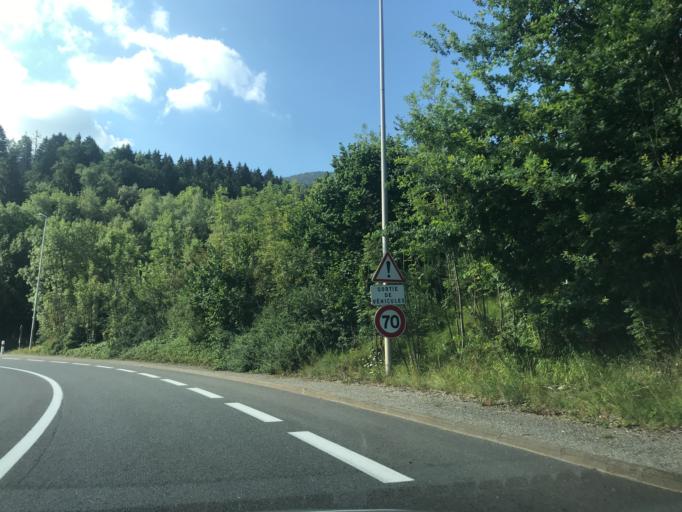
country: FR
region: Rhone-Alpes
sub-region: Departement de la Haute-Savoie
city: Villaz
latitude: 45.9206
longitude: 6.1806
